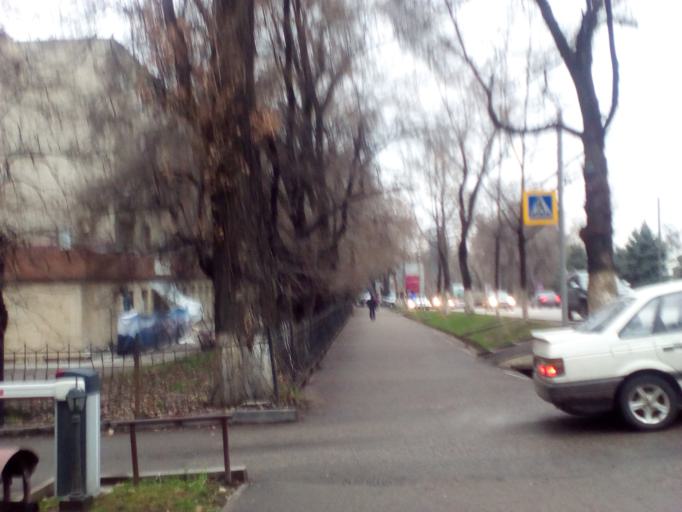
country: KZ
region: Almaty Qalasy
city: Almaty
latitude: 43.2235
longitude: 76.9625
